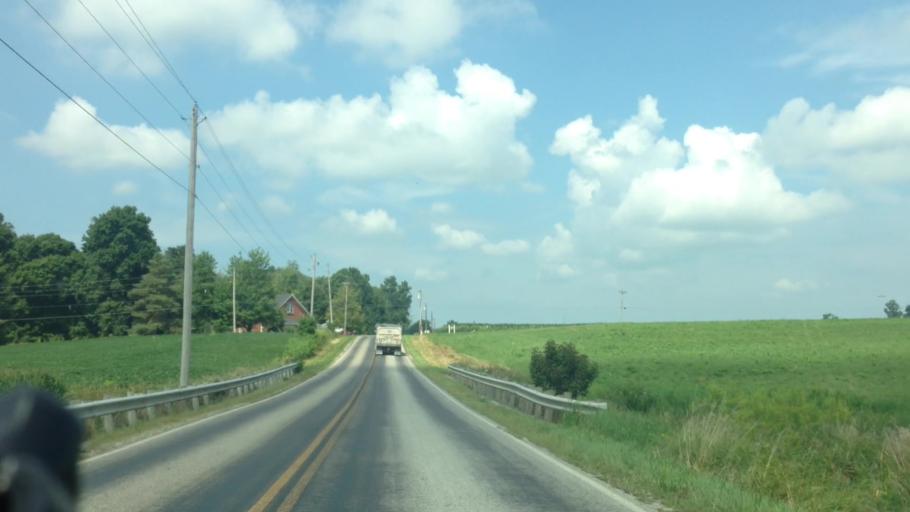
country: US
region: Ohio
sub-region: Wayne County
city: Orrville
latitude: 40.8720
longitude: -81.7041
